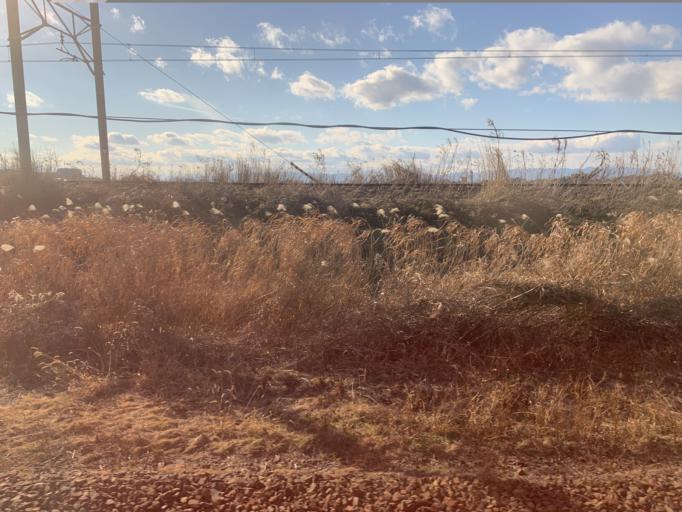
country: JP
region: Aichi
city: Ichinomiya
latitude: 35.2699
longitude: 136.8128
